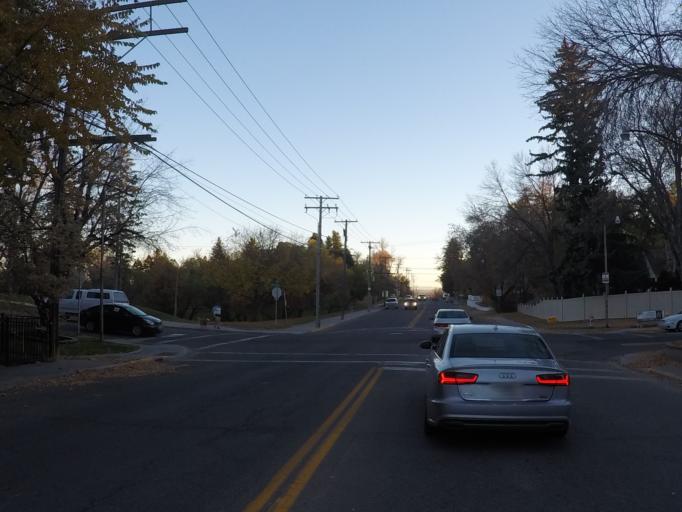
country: US
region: Montana
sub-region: Yellowstone County
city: Billings
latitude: 45.7902
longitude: -108.5279
